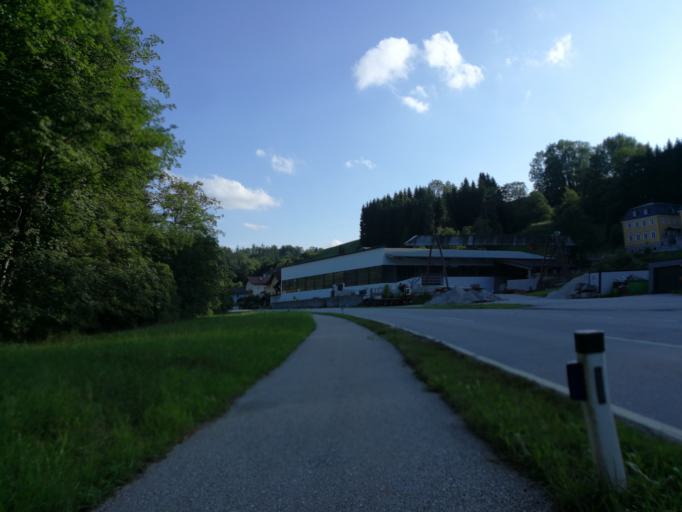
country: AT
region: Salzburg
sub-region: Politischer Bezirk Salzburg-Umgebung
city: Plainfeld
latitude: 47.8354
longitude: 13.1652
